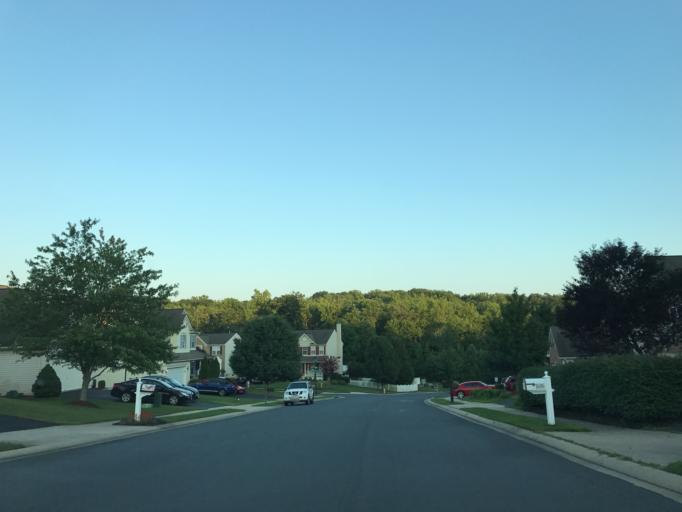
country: US
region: Maryland
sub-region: Harford County
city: Joppatowne
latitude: 39.4375
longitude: -76.3700
